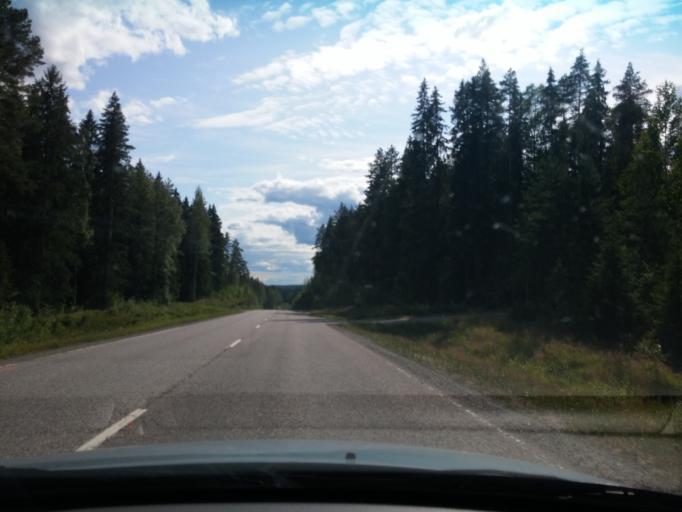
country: FI
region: Central Finland
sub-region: Keuruu
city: Keuruu
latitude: 62.2855
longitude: 24.6970
